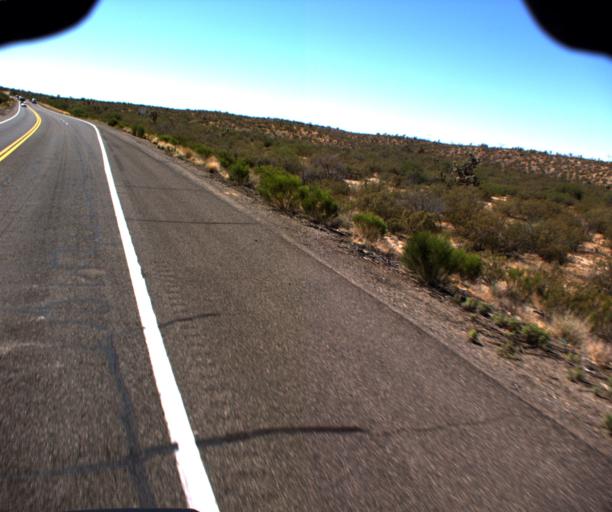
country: US
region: Arizona
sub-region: Yavapai County
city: Congress
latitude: 34.2035
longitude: -113.0632
